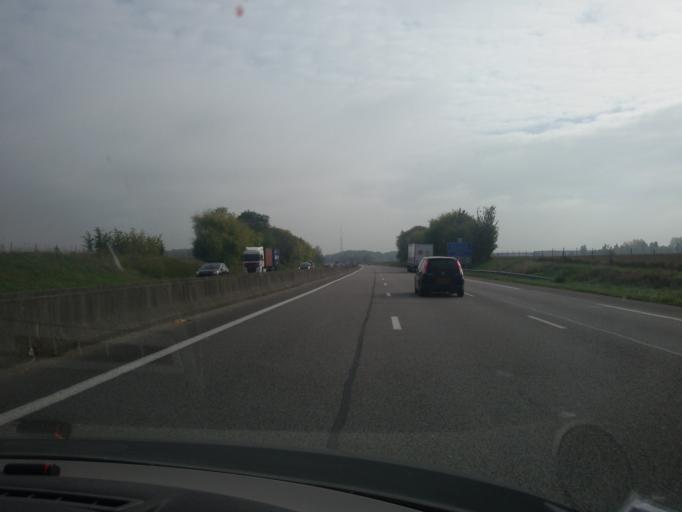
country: FR
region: Haute-Normandie
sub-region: Departement de l'Eure
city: Saint-Aubin-sur-Gaillon
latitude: 49.1151
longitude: 1.3338
